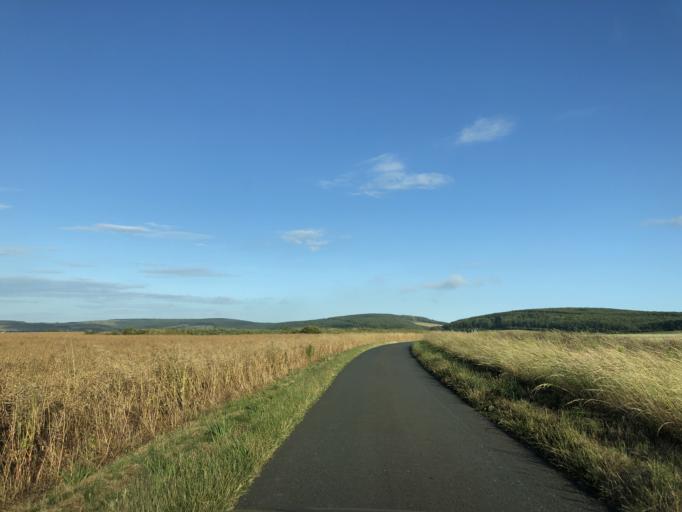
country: GB
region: England
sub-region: Isle of Wight
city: Yarmouth
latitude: 50.6794
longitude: -1.4612
